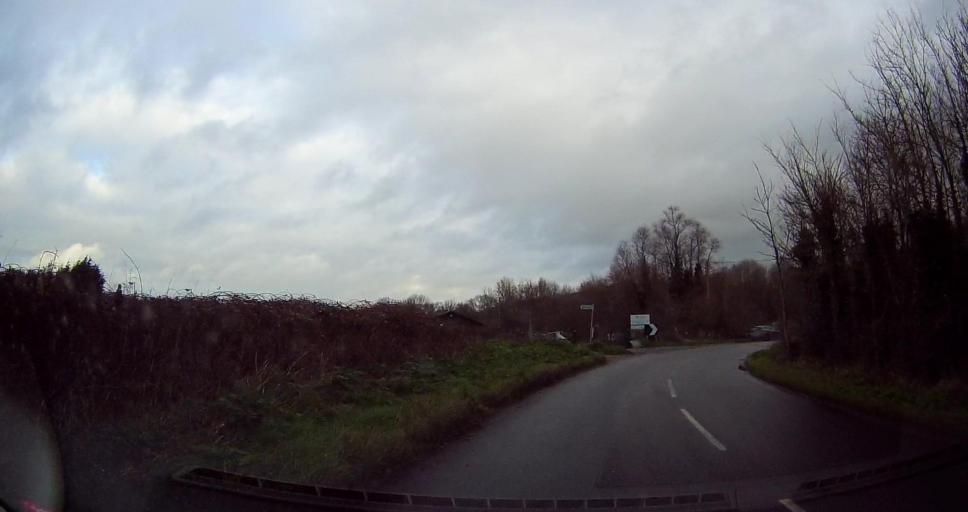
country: GB
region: England
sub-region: Medway
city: Rochester
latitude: 51.4077
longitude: 0.5180
